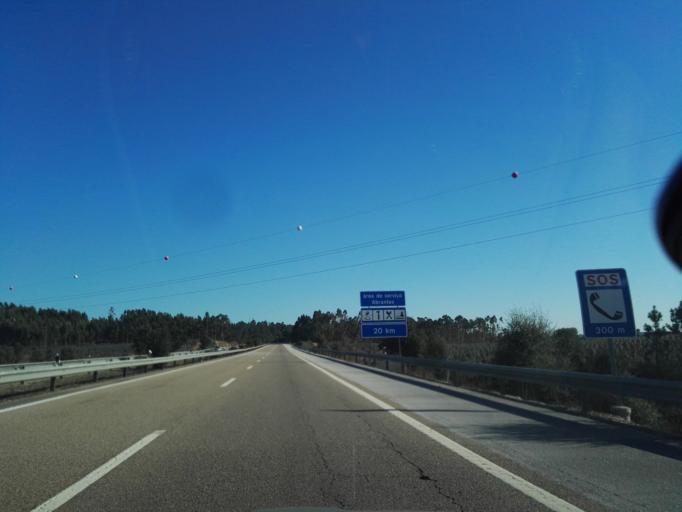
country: PT
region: Santarem
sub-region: Constancia
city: Constancia
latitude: 39.4853
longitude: -8.3774
